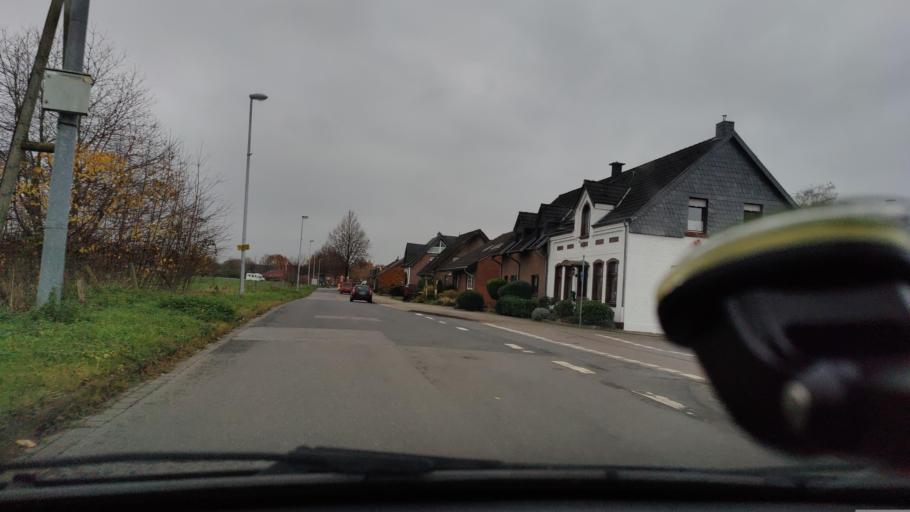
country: DE
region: North Rhine-Westphalia
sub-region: Regierungsbezirk Dusseldorf
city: Kamp-Lintfort
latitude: 51.5383
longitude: 6.5452
